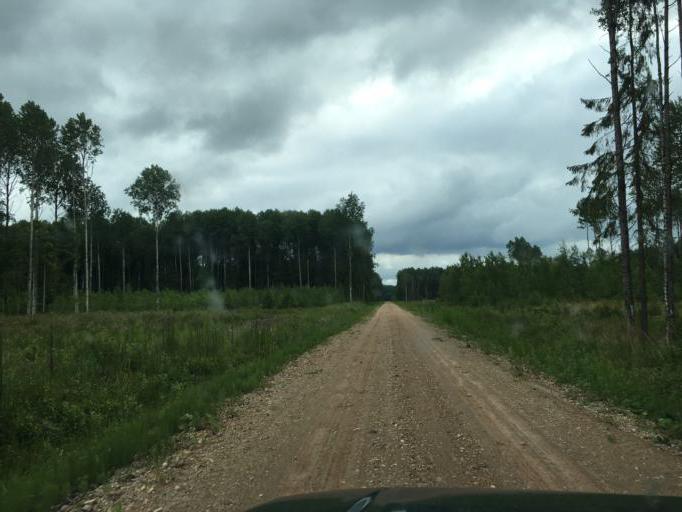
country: LV
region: Vilaka
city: Vilaka
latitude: 57.3872
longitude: 27.5044
